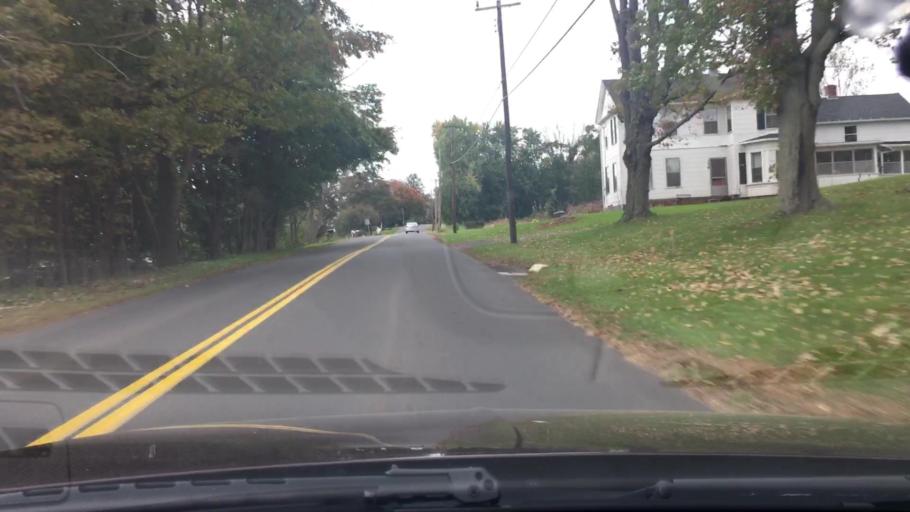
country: US
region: Connecticut
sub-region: Tolland County
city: Ellington
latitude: 41.9243
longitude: -72.4766
